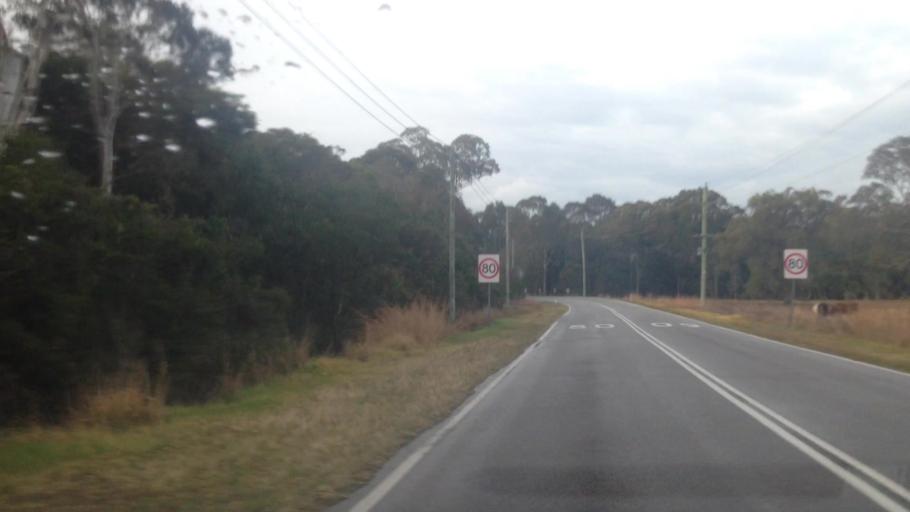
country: AU
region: New South Wales
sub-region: Wyong Shire
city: Charmhaven
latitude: -33.1656
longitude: 151.4774
